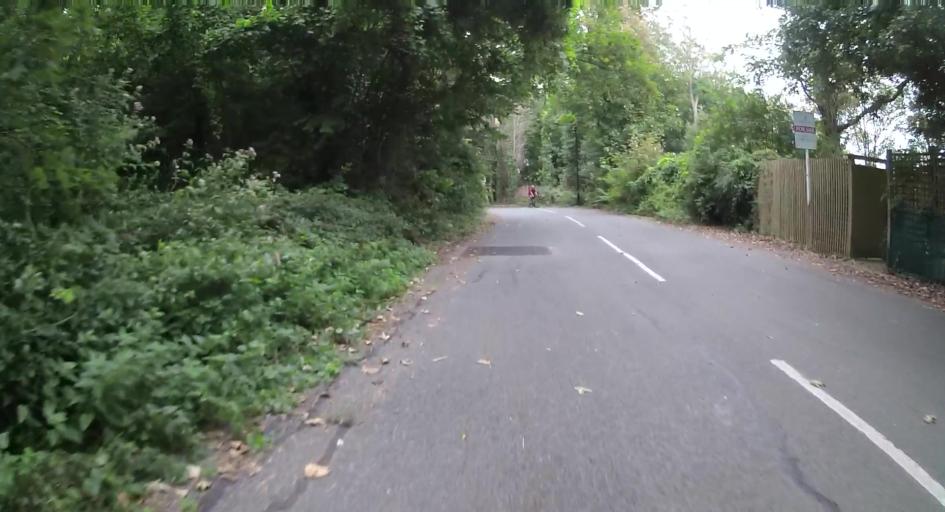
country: GB
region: England
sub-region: Isle of Wight
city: Niton
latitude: 50.5845
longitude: -1.2551
